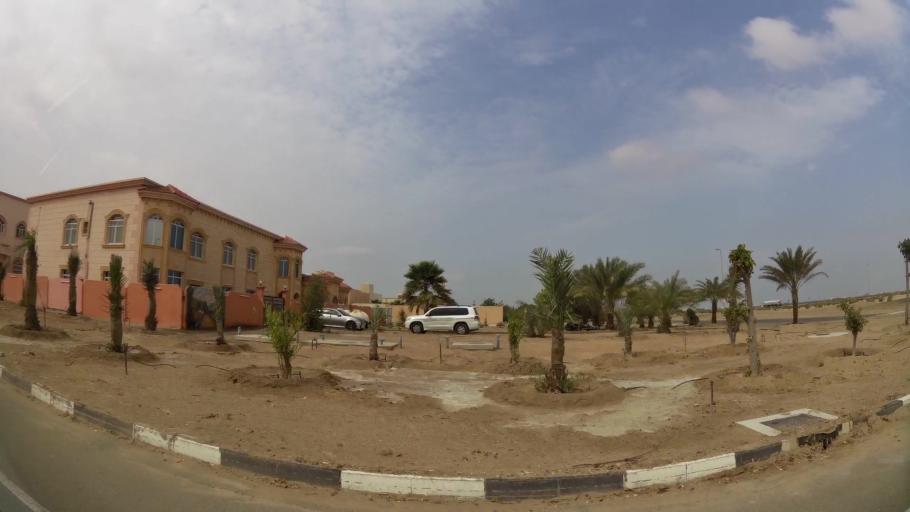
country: AE
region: Abu Dhabi
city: Abu Dhabi
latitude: 24.6336
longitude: 54.6927
